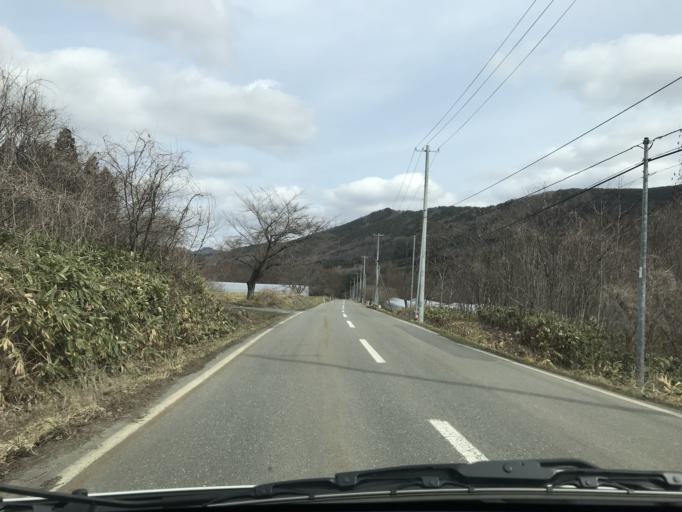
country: JP
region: Iwate
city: Kitakami
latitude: 39.2642
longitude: 141.3184
